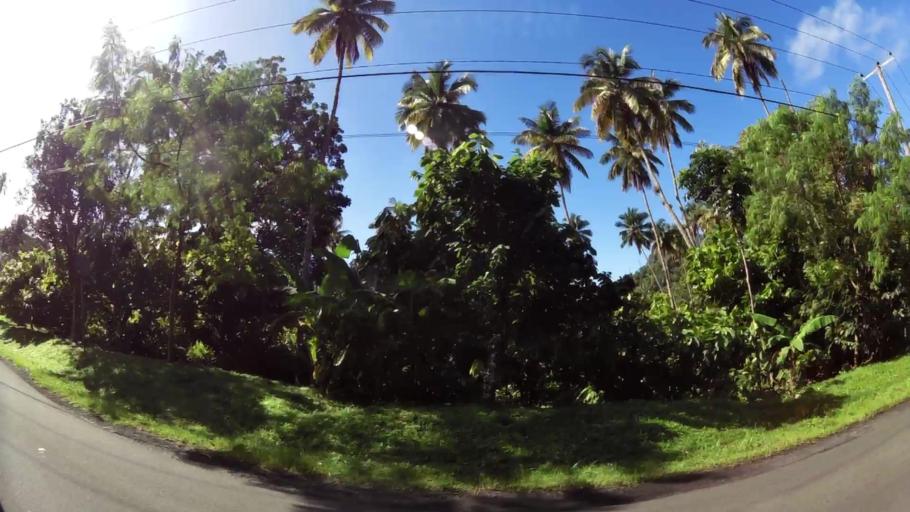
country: LC
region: Soufriere
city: Soufriere
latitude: 13.8212
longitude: -61.0447
